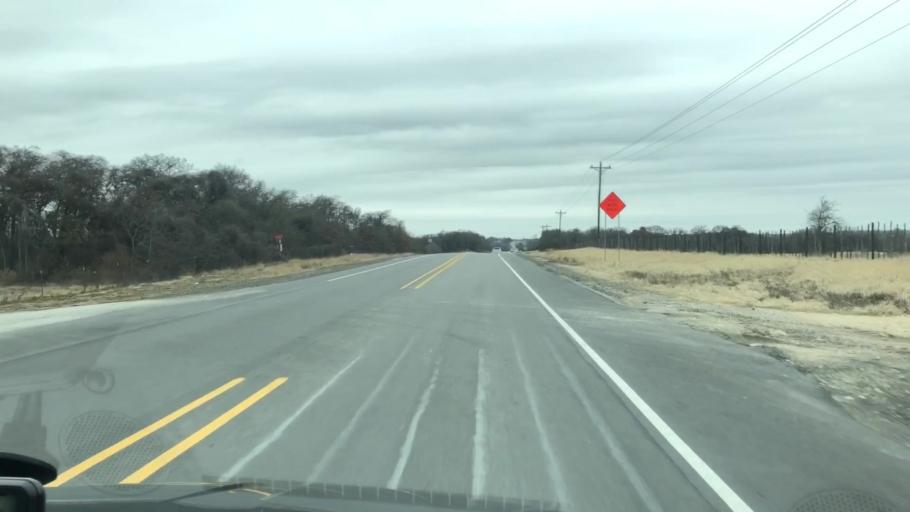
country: US
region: Texas
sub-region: Erath County
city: Stephenville
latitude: 32.1218
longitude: -98.1252
